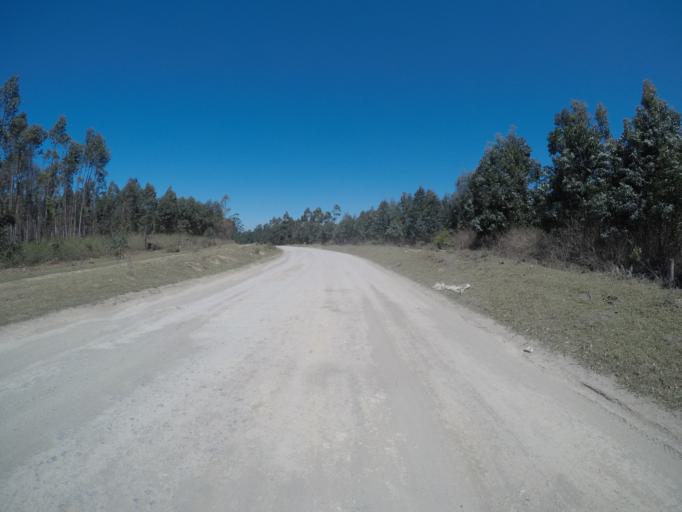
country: ZA
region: Eastern Cape
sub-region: OR Tambo District Municipality
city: Libode
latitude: -31.9527
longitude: 29.0235
